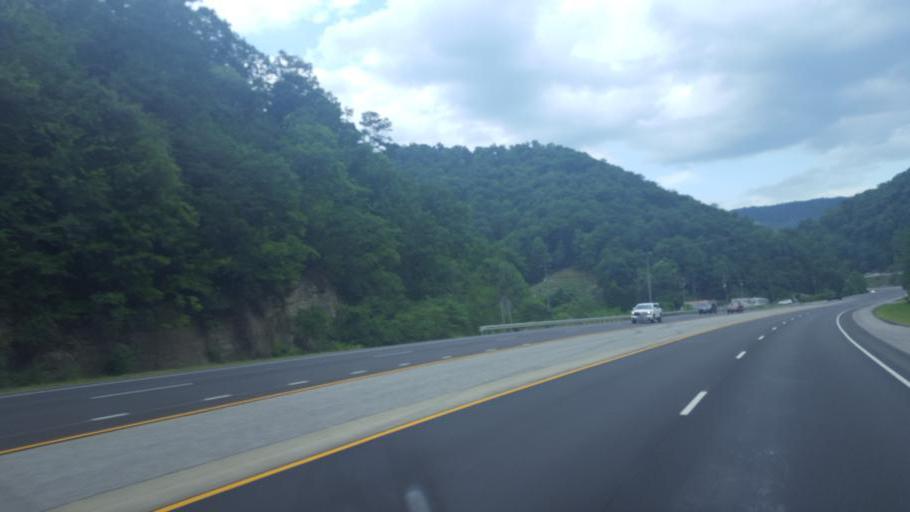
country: US
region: Kentucky
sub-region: Pike County
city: Pikeville
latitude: 37.3173
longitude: -82.5501
